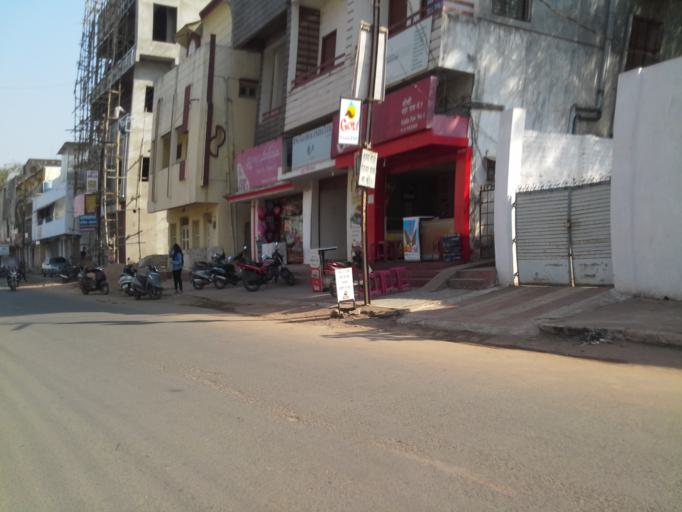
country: IN
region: Maharashtra
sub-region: Gondiya
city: Gondia
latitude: 21.4641
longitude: 80.1903
